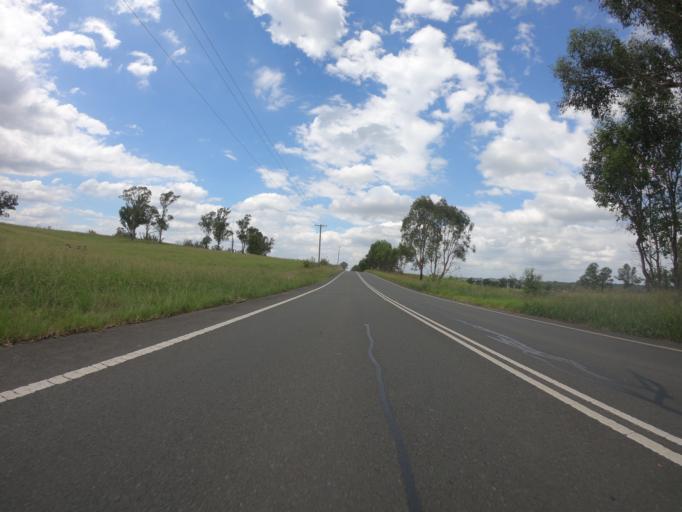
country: AU
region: New South Wales
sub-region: Liverpool
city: Luddenham
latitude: -33.8399
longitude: 150.7449
